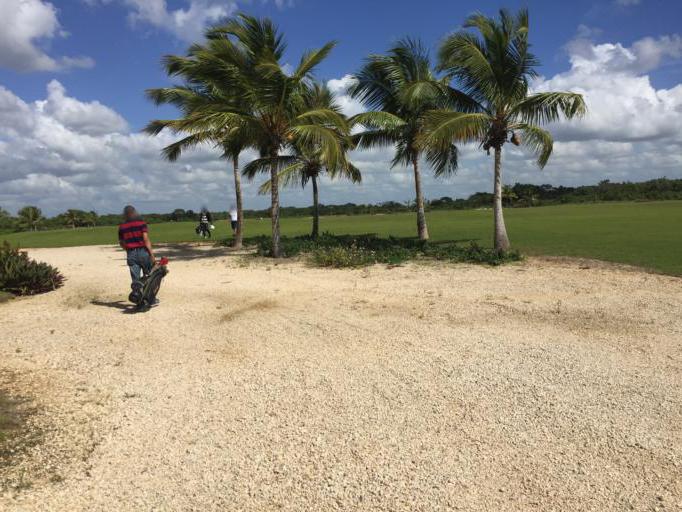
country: DO
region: Santo Domingo
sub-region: Santo Domingo
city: Boca Chica
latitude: 18.4691
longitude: -69.6535
